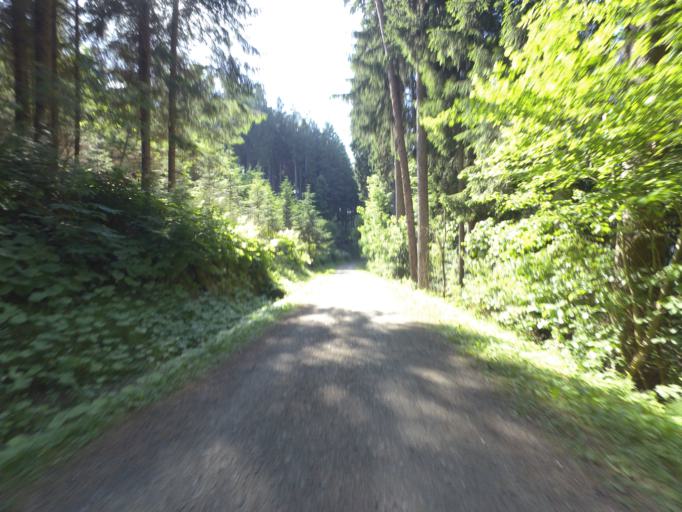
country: AT
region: Carinthia
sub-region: Politischer Bezirk Spittal an der Drau
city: Millstatt
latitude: 46.7949
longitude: 13.5638
